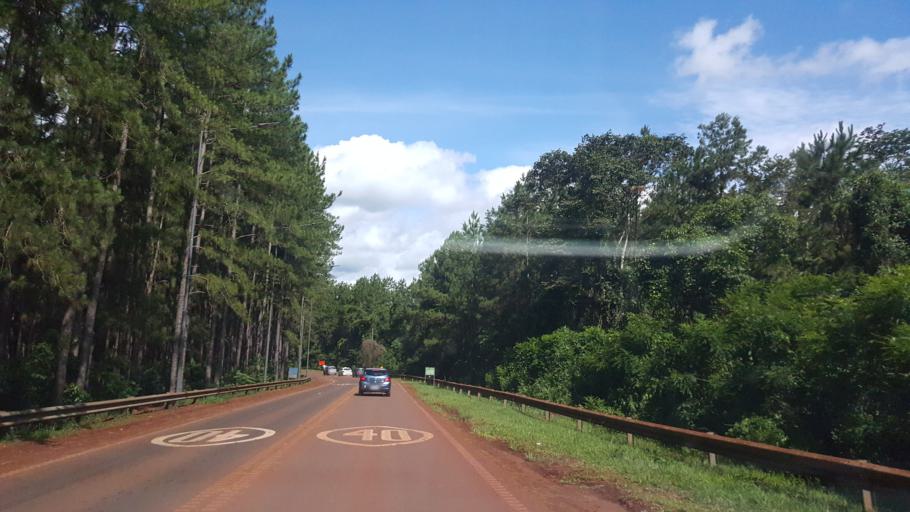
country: AR
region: Misiones
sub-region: Departamento de Iguazu
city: Puerto Iguazu
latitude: -25.7315
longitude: -54.4739
